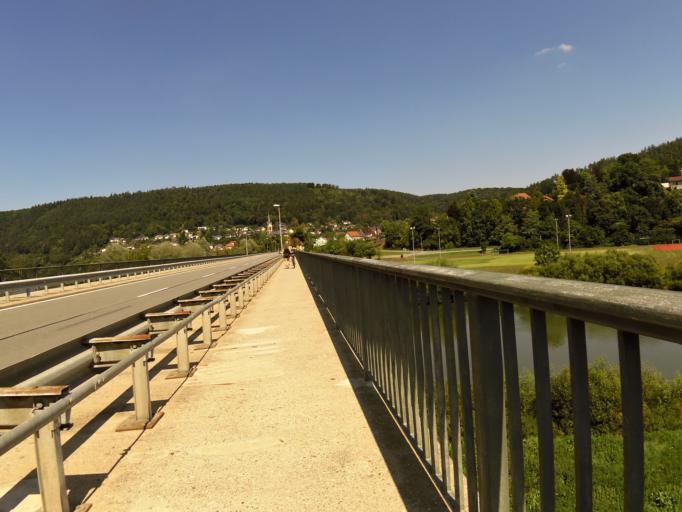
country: DE
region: Baden-Wuerttemberg
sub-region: Karlsruhe Region
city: Neckargerach
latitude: 49.3933
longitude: 9.0703
